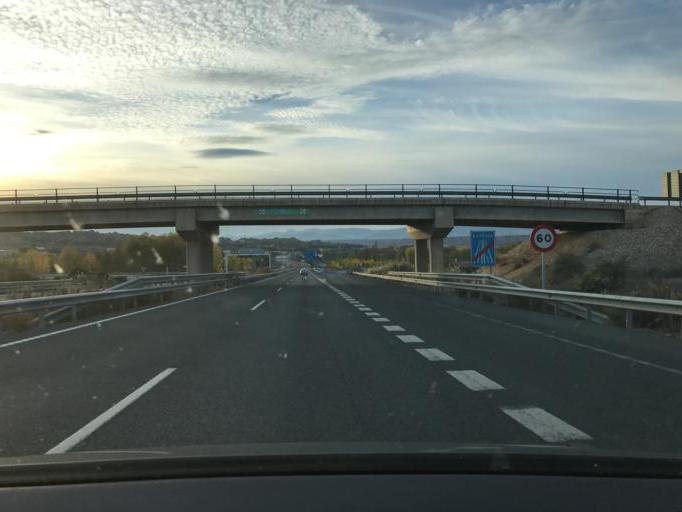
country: ES
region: Andalusia
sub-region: Provincia de Granada
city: Guadix
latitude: 37.3192
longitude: -3.1369
